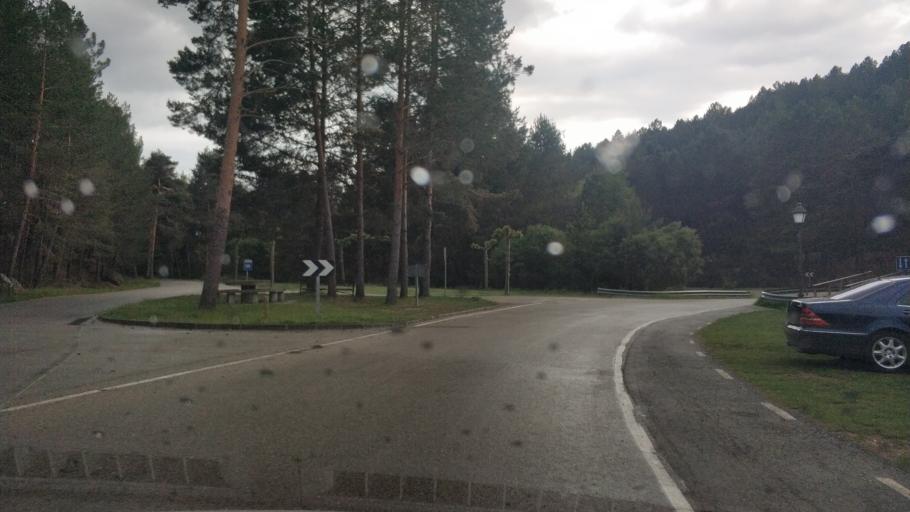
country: ES
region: Castille and Leon
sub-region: Provincia de Soria
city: San Leonardo de Yague
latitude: 41.8375
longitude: -3.0655
